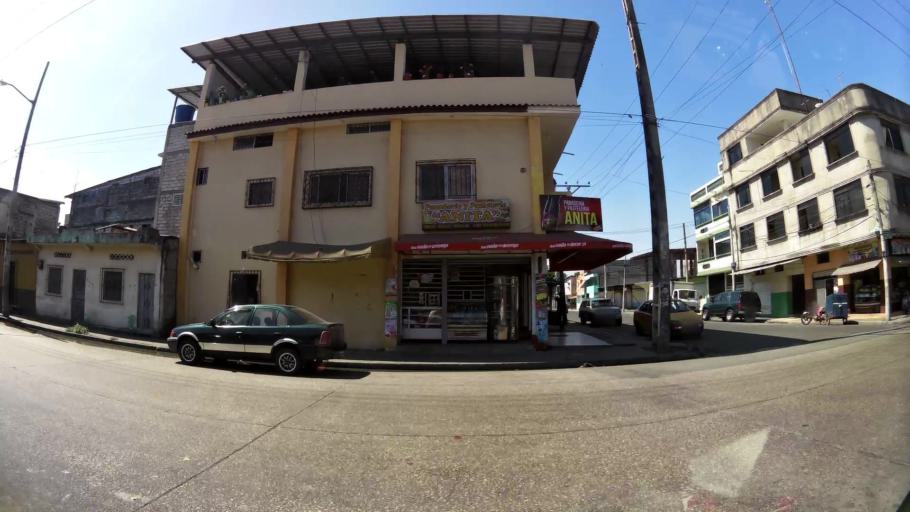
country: EC
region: Guayas
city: Guayaquil
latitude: -2.2269
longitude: -79.9434
